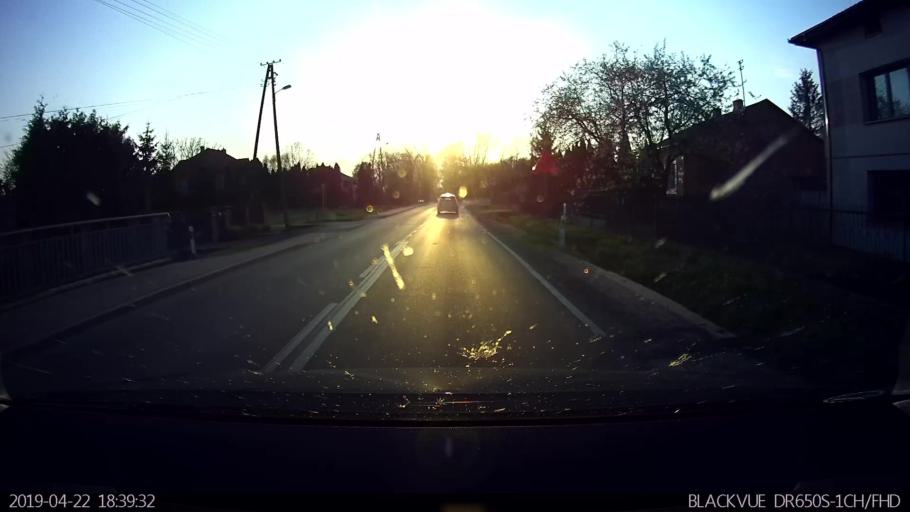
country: PL
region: Masovian Voivodeship
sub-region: Powiat wolominski
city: Dabrowka
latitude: 52.4418
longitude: 21.2854
